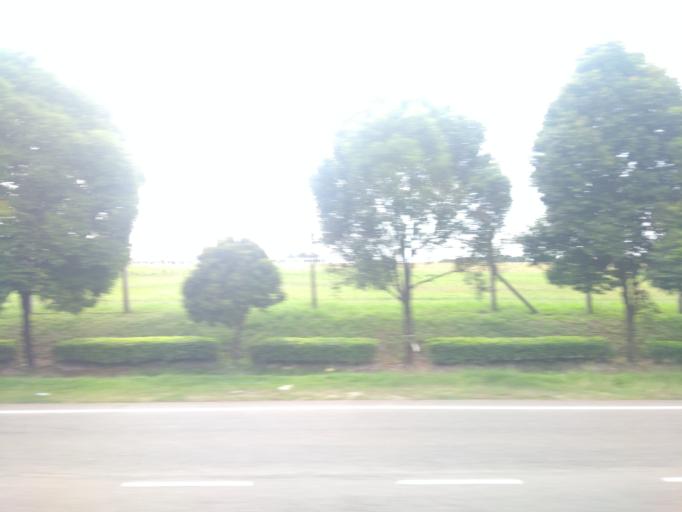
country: MY
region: Melaka
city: Batu Berendam
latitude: 2.2687
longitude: 102.2567
